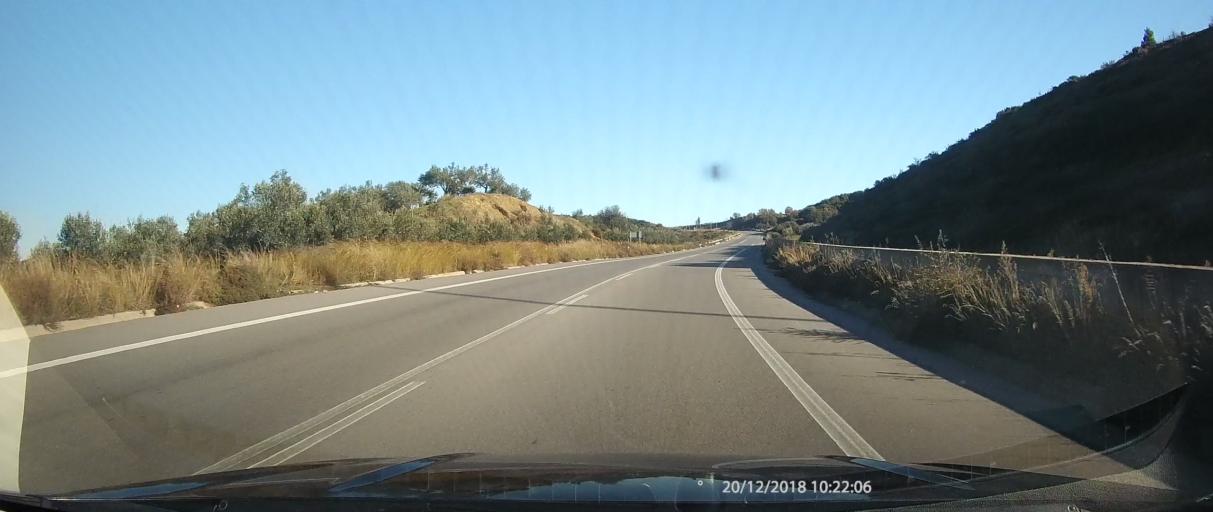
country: GR
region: Peloponnese
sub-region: Nomos Lakonias
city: Magoula
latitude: 37.1699
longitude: 22.4256
